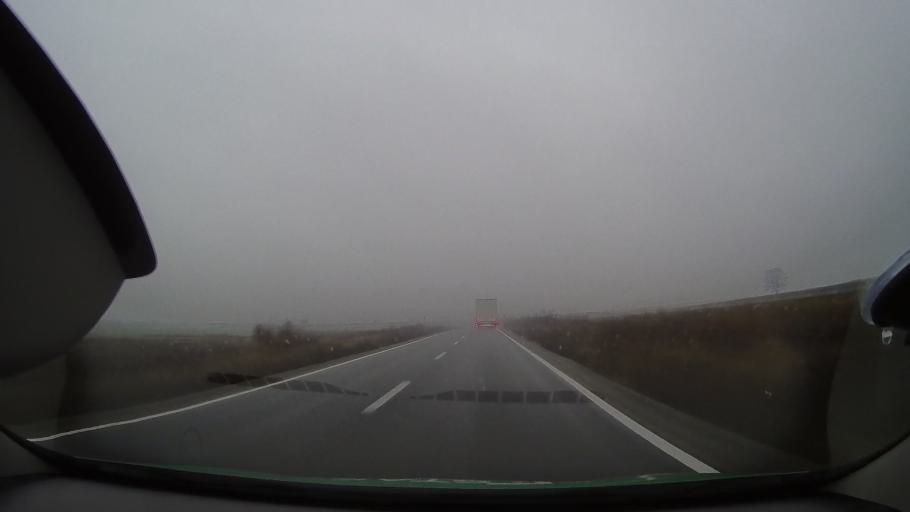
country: RO
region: Bihor
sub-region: Comuna Olcea
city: Olcea
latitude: 46.6742
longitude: 21.9650
